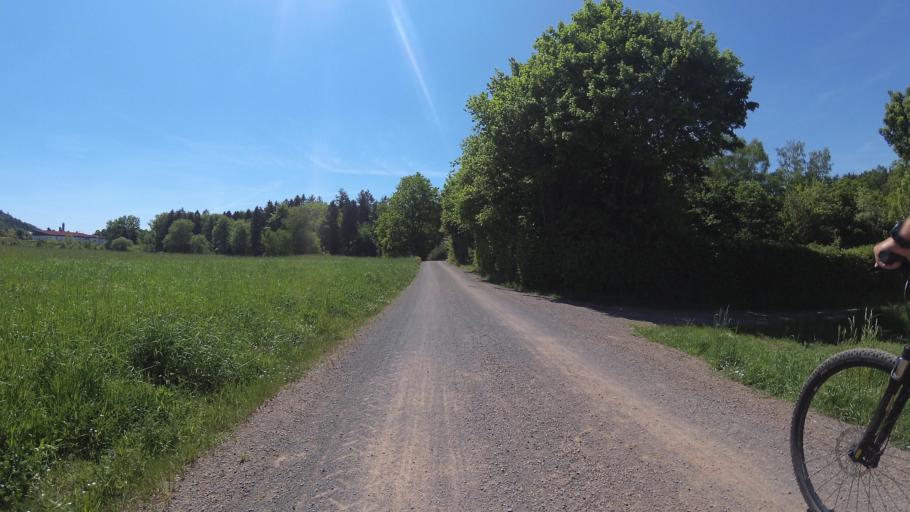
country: DE
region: Saarland
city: Kirkel
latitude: 49.2953
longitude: 7.2398
